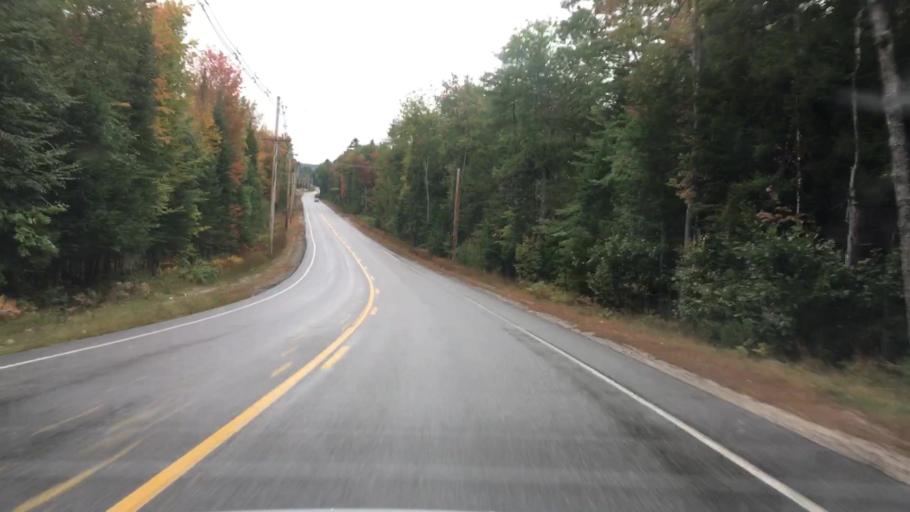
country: US
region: Maine
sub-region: Cumberland County
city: Raymond
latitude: 43.9822
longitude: -70.5363
